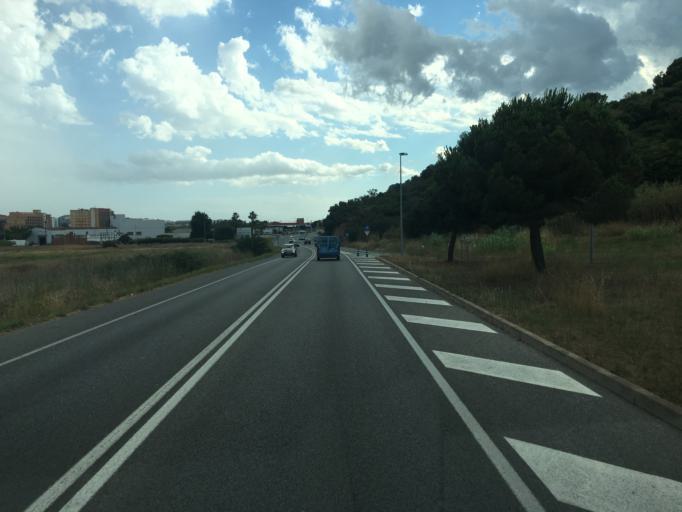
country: ES
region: Catalonia
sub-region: Provincia de Barcelona
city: Malgrat de Mar
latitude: 41.6447
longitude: 2.7287
